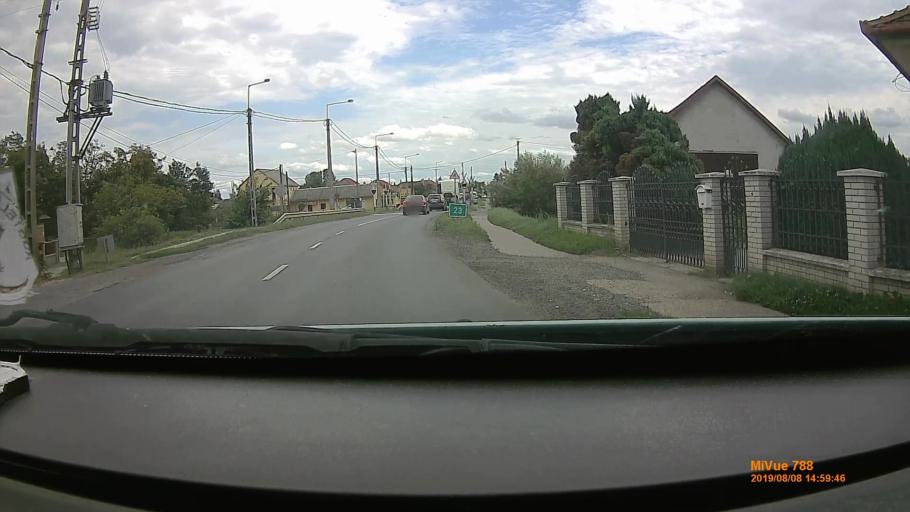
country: HU
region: Szabolcs-Szatmar-Bereg
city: Kocsord
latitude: 47.9417
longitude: 22.3732
